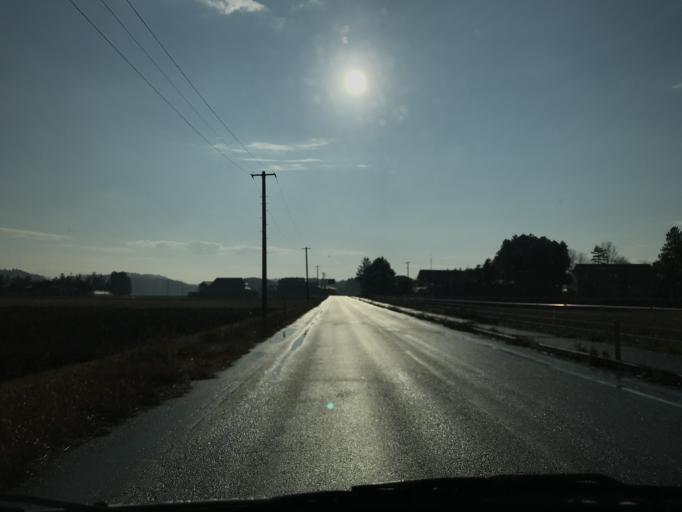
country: JP
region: Iwate
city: Ichinoseki
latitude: 38.7706
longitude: 141.1797
